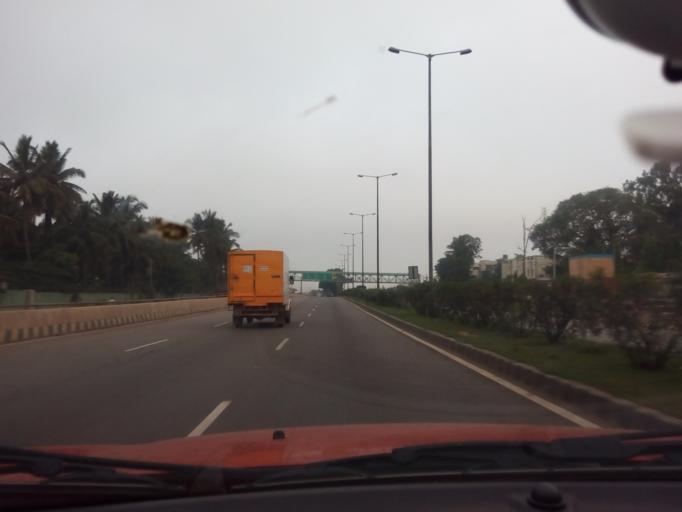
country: IN
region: Karnataka
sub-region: Bangalore Rural
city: Nelamangala
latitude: 13.0539
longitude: 77.4828
